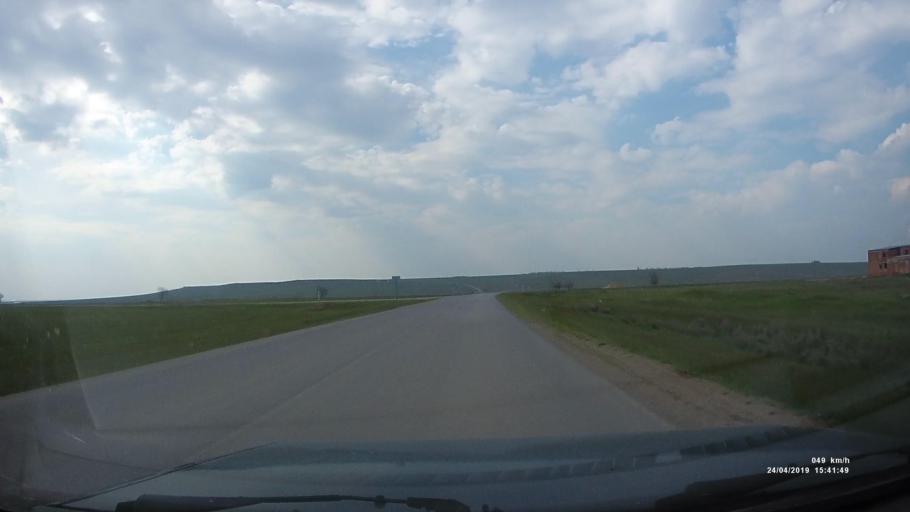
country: RU
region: Kalmykiya
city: Yashalta
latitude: 46.5712
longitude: 42.7943
